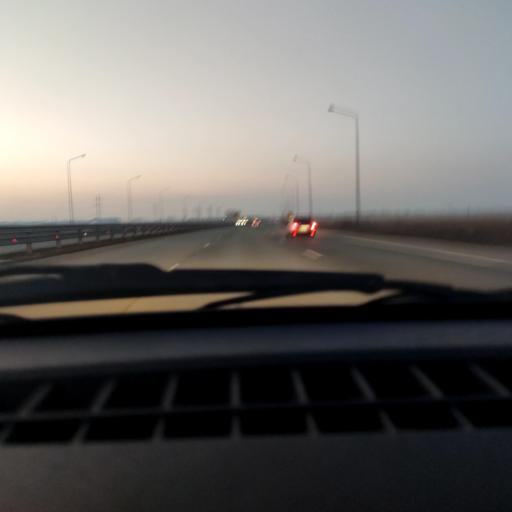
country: RU
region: Bashkortostan
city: Asanovo
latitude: 54.8948
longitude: 55.6408
